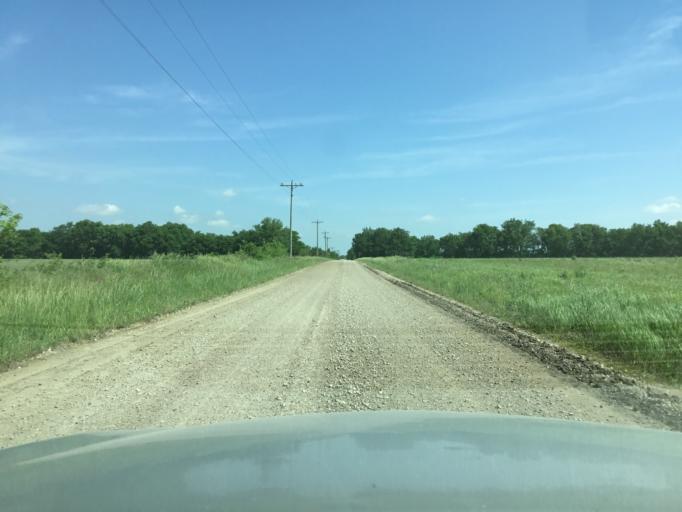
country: US
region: Kansas
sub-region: Labette County
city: Oswego
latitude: 37.1687
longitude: -95.1399
